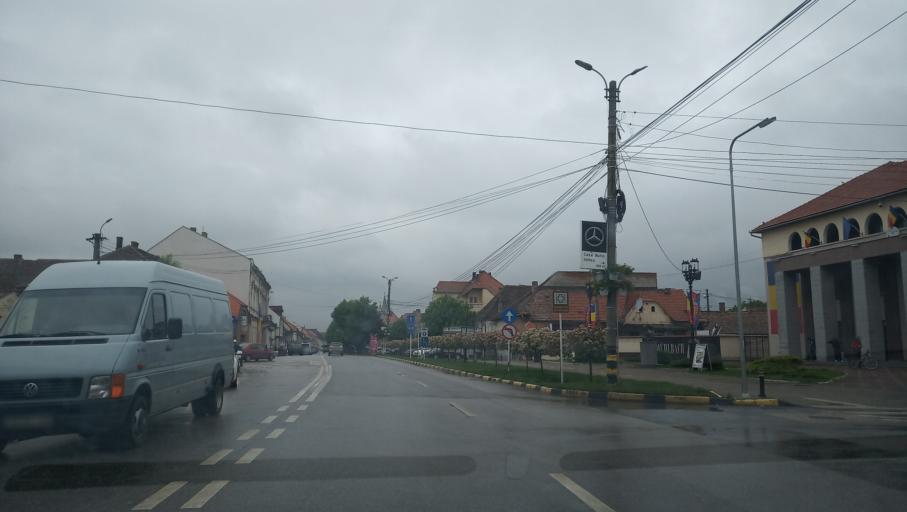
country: RO
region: Alba
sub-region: Municipiul Sebes
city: Sebes
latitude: 45.9564
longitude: 23.5742
